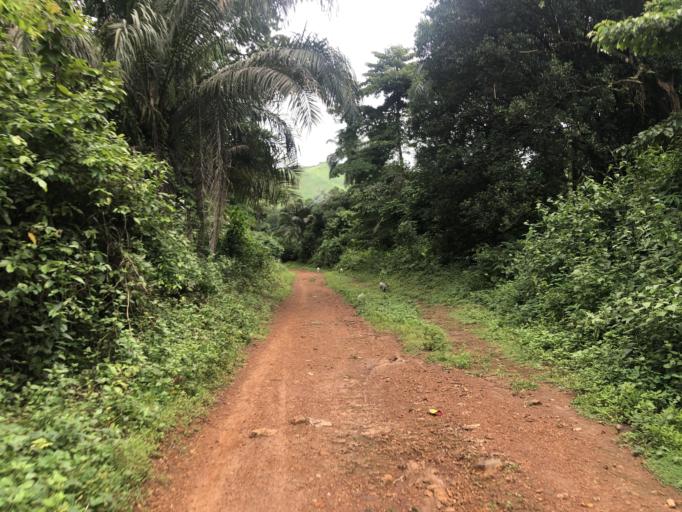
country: SL
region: Northern Province
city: Bumbuna
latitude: 8.9932
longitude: -11.7542
